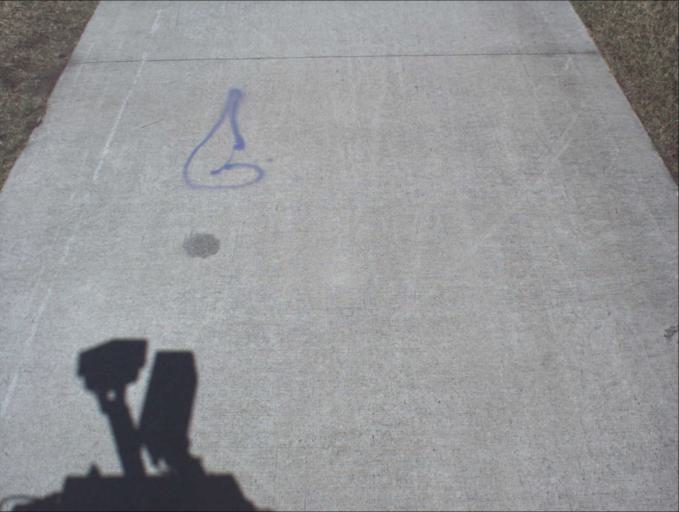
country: AU
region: Queensland
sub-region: Logan
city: Beenleigh
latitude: -27.7193
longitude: 153.1987
